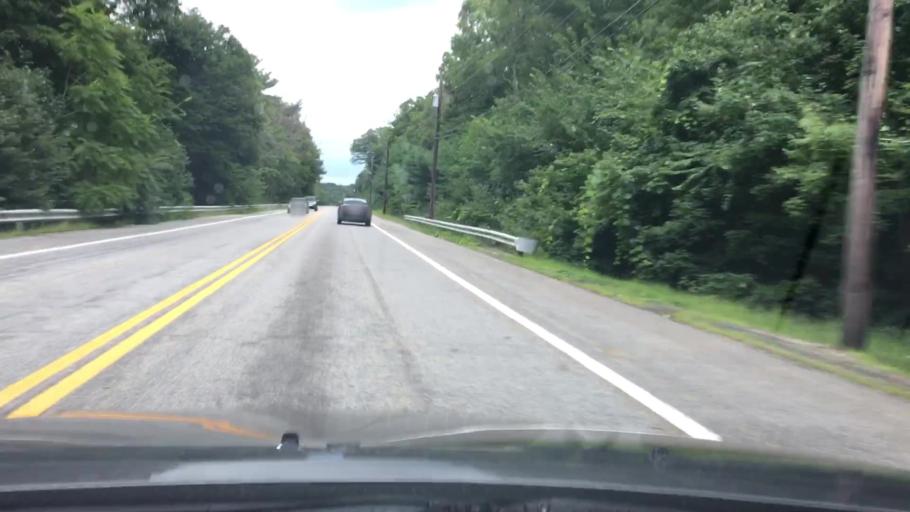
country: US
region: Rhode Island
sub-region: Providence County
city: Cumberland
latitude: 42.0085
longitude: -71.4270
